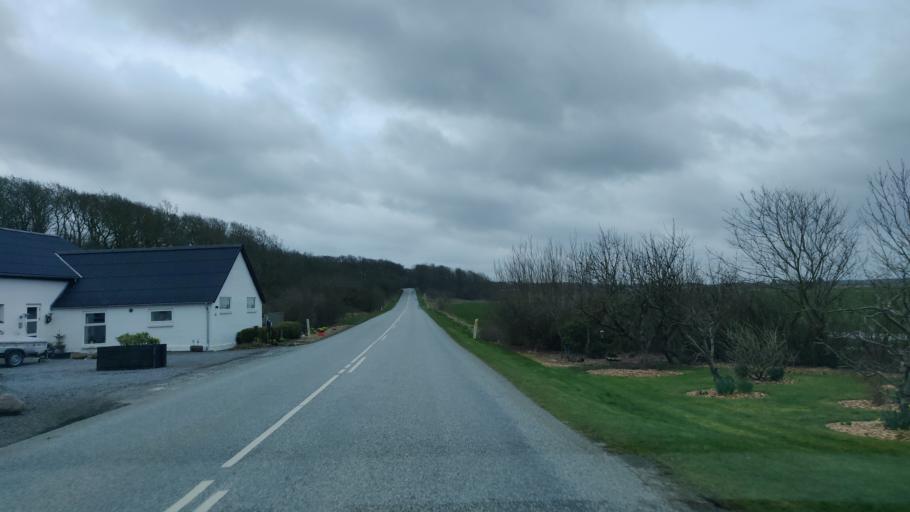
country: DK
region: Central Jutland
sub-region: Skive Kommune
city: Hojslev
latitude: 56.5613
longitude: 9.2483
